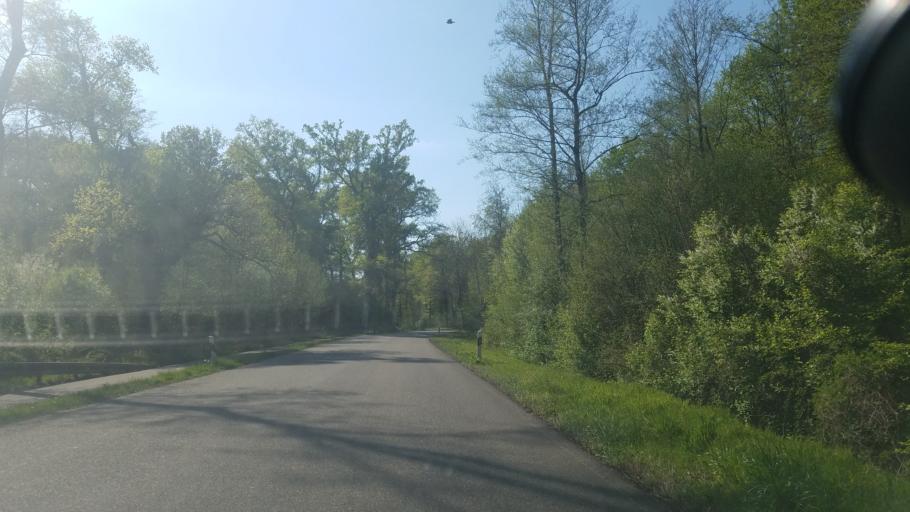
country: DE
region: Baden-Wuerttemberg
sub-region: Karlsruhe Region
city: Ottenhofen
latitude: 48.7649
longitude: 8.1214
